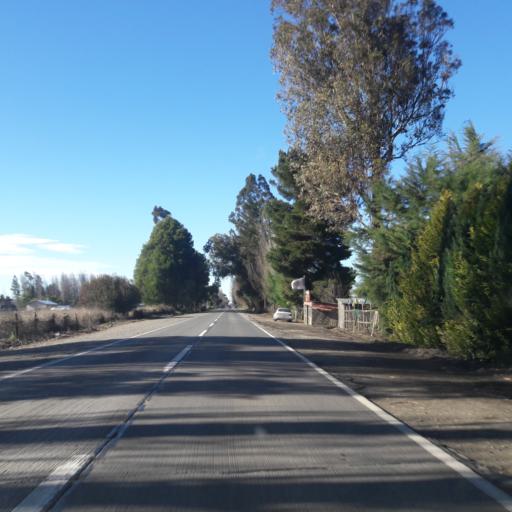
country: CL
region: Araucania
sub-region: Provincia de Malleco
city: Angol
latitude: -37.7612
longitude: -72.5691
